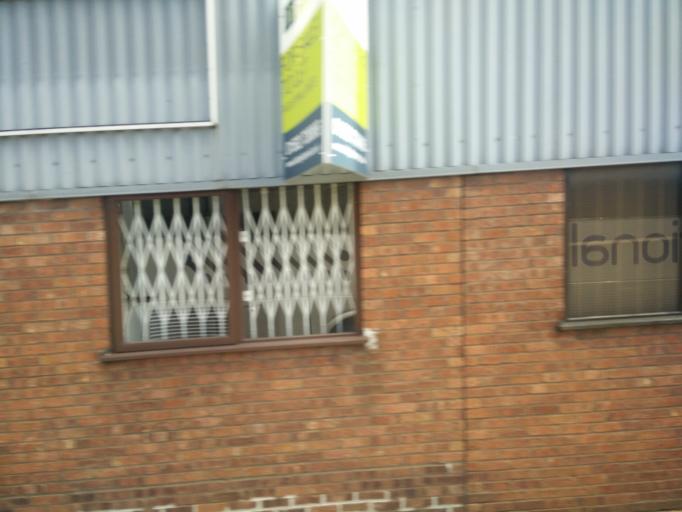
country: GB
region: England
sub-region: Luton
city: Luton
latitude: 51.8829
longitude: -0.4097
